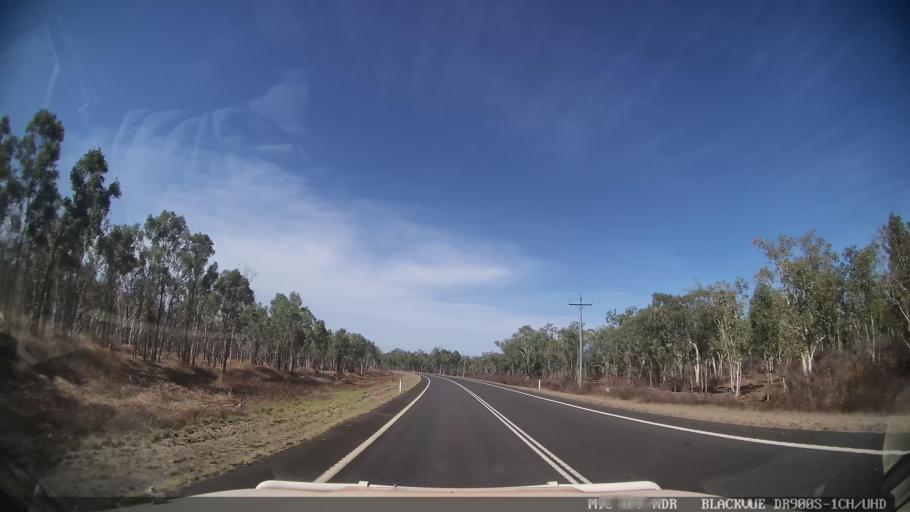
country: AU
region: Queensland
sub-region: Cook
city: Cooktown
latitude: -15.7889
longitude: 144.9491
